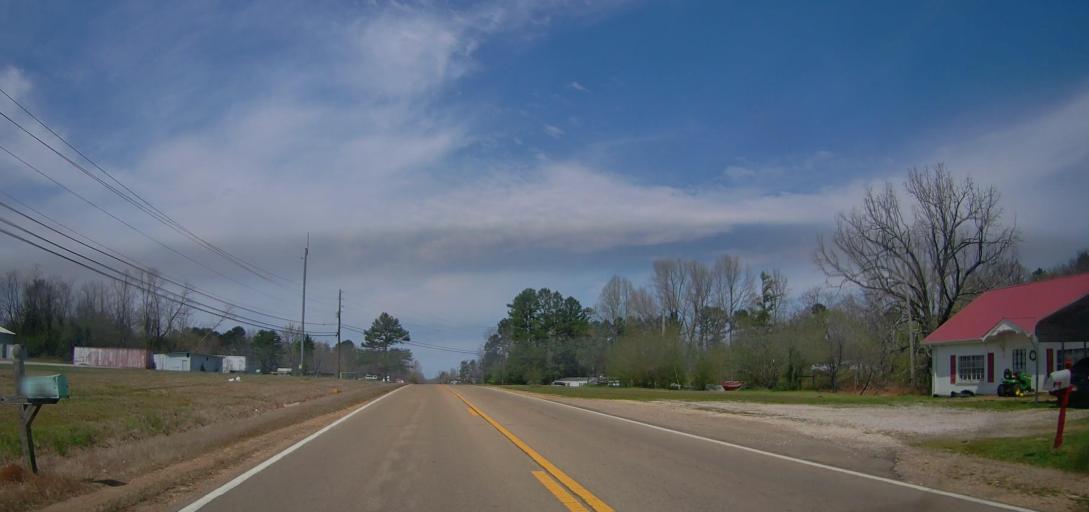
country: US
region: Mississippi
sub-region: Union County
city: New Albany
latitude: 34.4531
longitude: -88.9728
